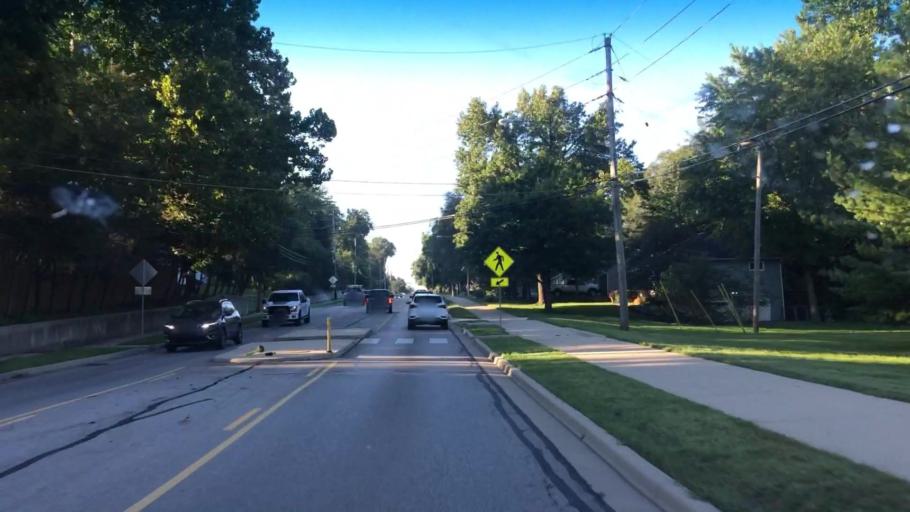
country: US
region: Kansas
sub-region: Johnson County
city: Mission
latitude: 39.0115
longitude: -94.6491
